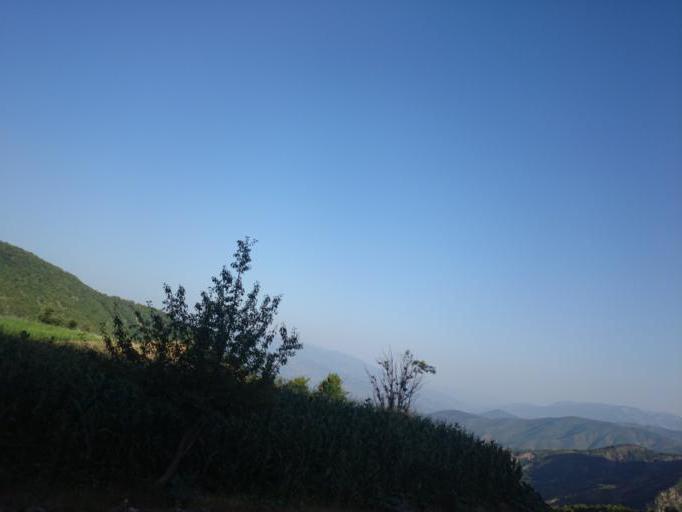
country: AL
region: Elbasan
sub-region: Rrethi i Librazhdit
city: Orenje
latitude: 41.2969
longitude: 20.1511
